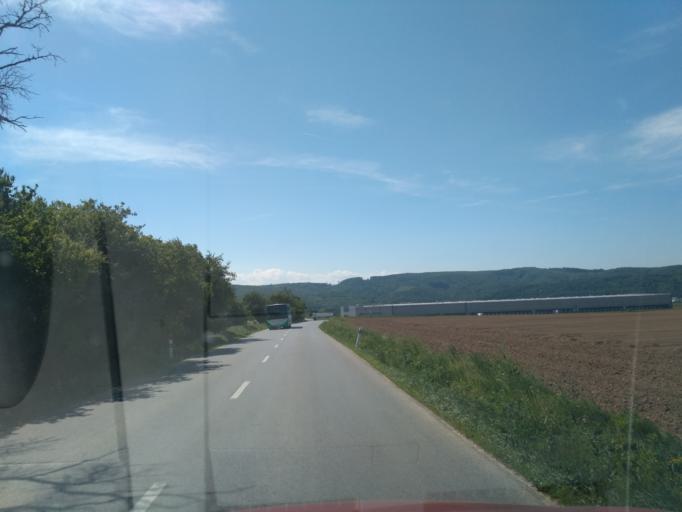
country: SK
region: Presovsky
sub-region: Okres Presov
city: Presov
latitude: 48.9505
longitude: 21.2711
